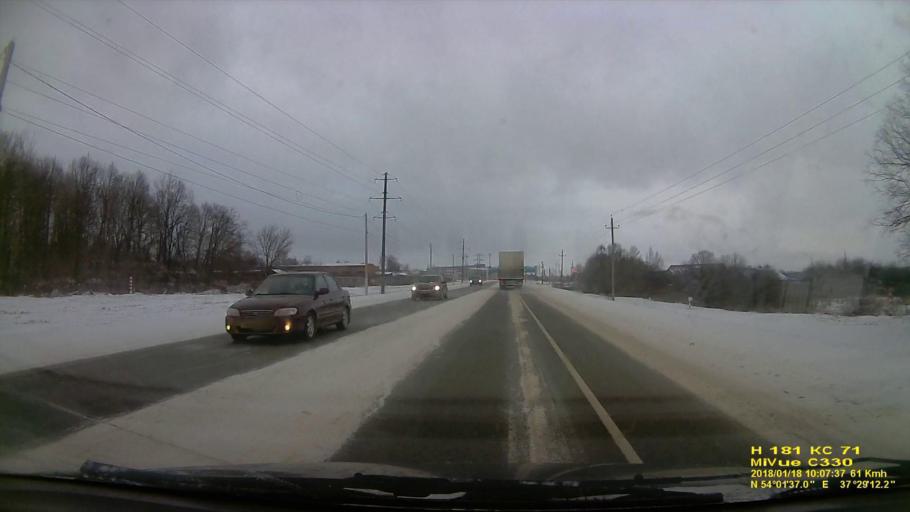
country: RU
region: Tula
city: Pervomayskiy
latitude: 54.0268
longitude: 37.4867
